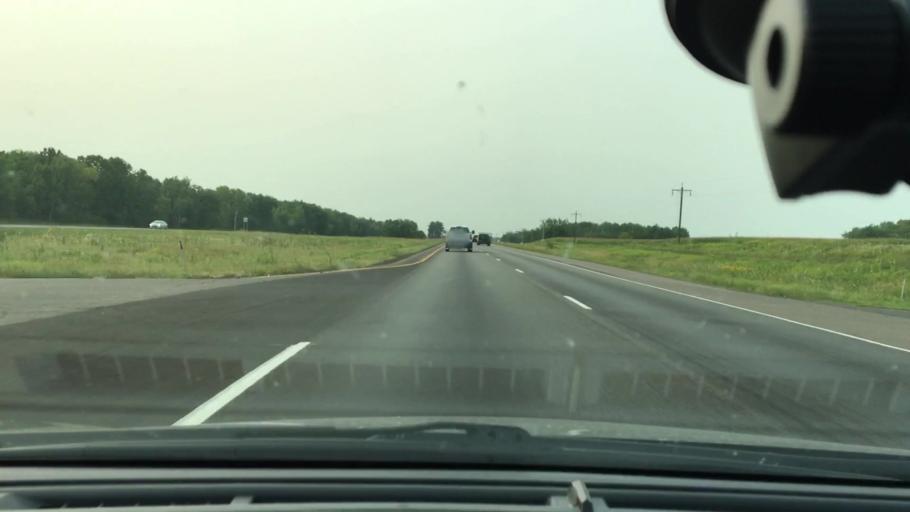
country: US
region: Minnesota
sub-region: Mille Lacs County
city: Milaca
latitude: 45.6661
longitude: -93.6289
